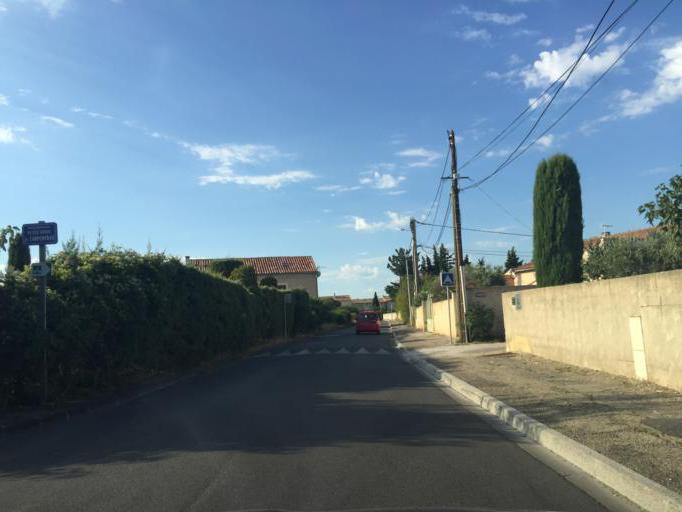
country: FR
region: Provence-Alpes-Cote d'Azur
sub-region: Departement du Vaucluse
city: Pernes-les-Fontaines
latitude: 44.0045
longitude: 5.0563
